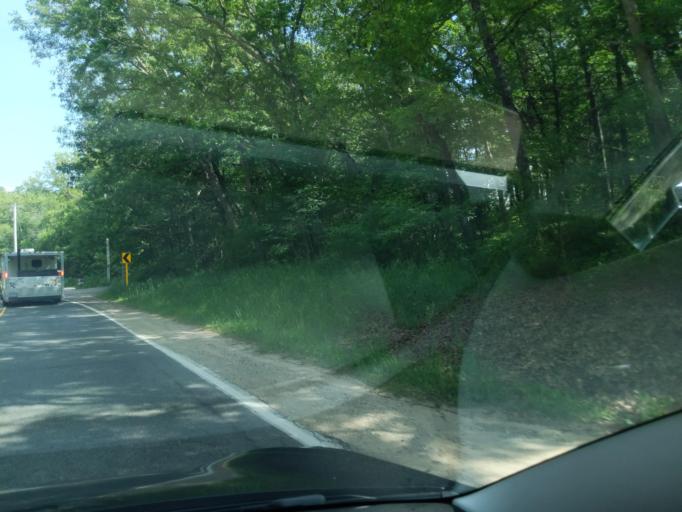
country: US
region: Michigan
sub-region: Muskegon County
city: Lakewood Club
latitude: 43.4046
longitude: -86.2576
